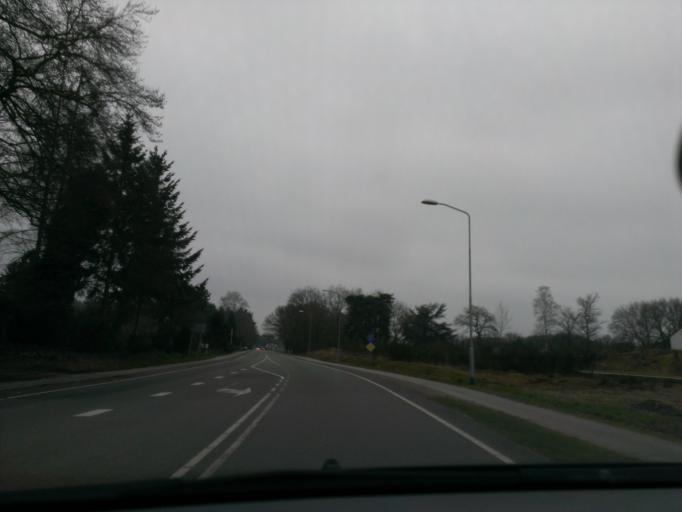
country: NL
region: Gelderland
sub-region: Gemeente Hattem
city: Hattem
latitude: 52.4382
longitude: 6.0710
